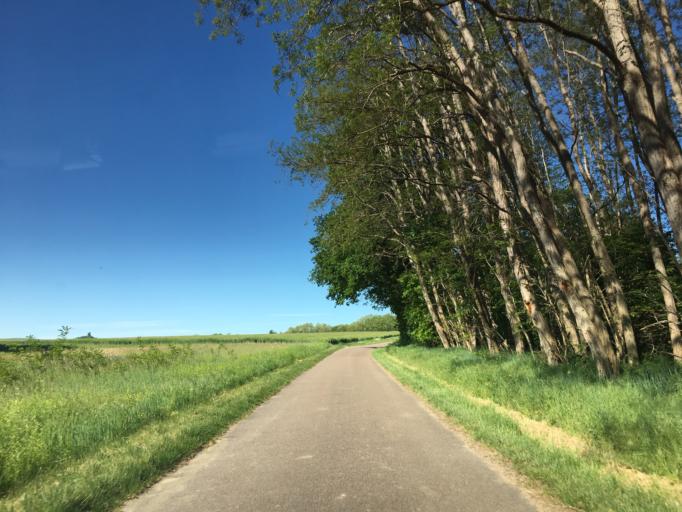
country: FR
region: Bourgogne
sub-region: Departement de l'Yonne
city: Aillant-sur-Tholon
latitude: 47.8217
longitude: 3.3661
